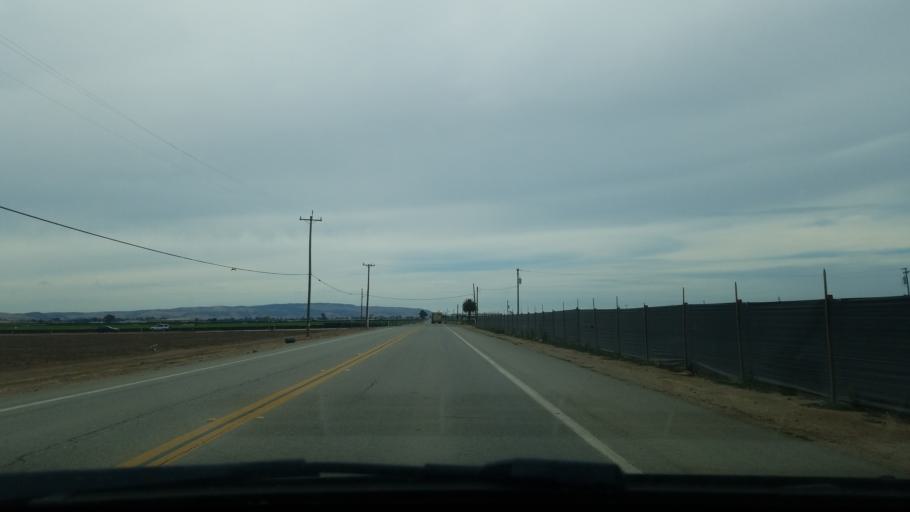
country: US
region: California
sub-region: Santa Barbara County
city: Santa Maria
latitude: 34.9235
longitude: -120.3813
